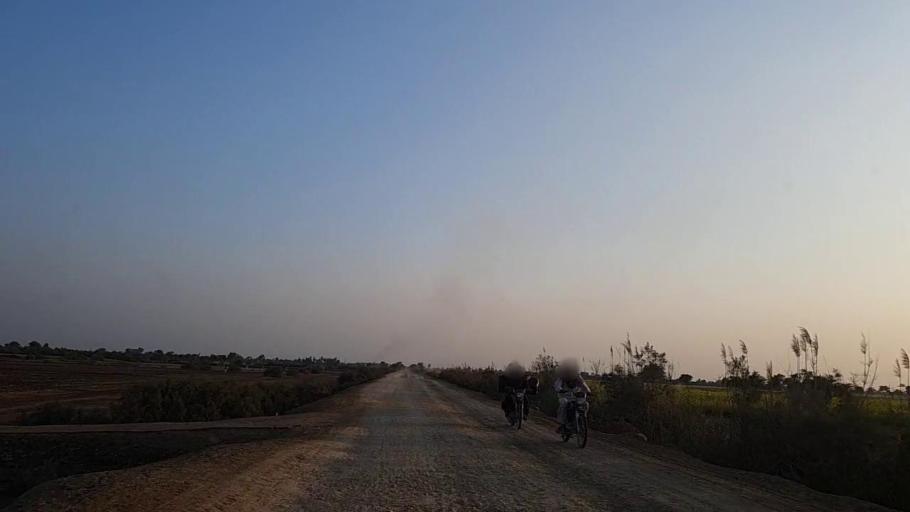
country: PK
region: Sindh
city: Shahdadpur
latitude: 25.9760
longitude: 68.4973
